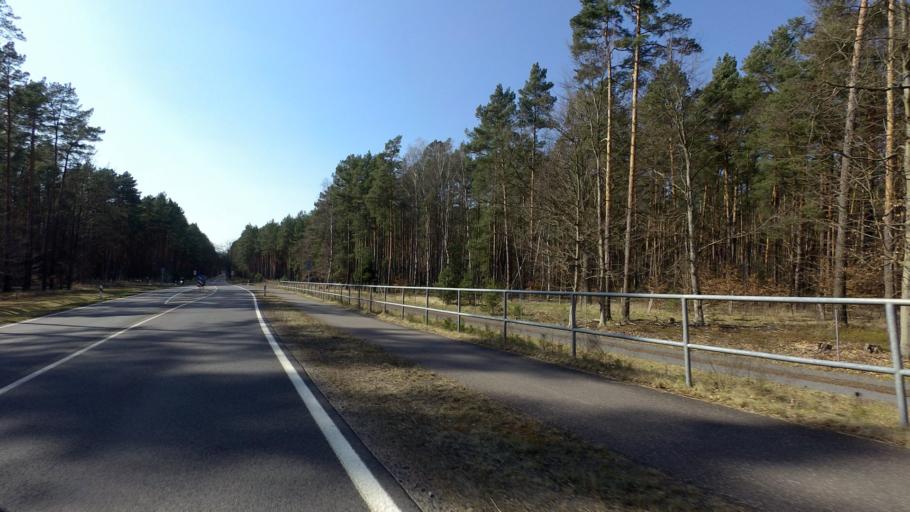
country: DE
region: Brandenburg
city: Oranienburg
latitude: 52.7933
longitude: 13.2275
